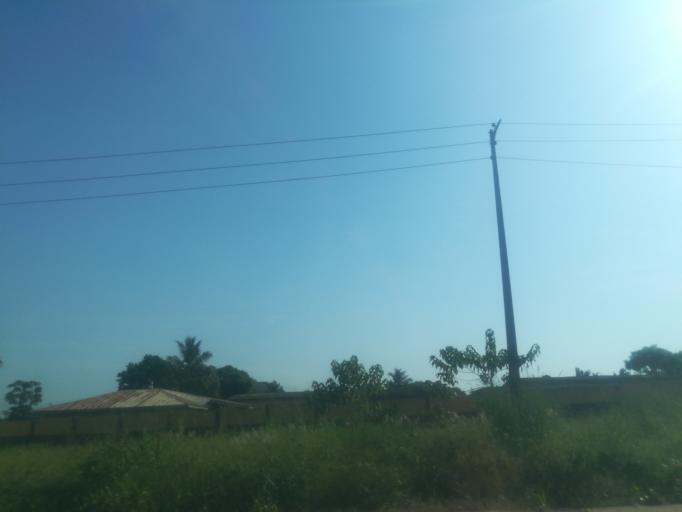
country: NG
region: Ogun
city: Abeokuta
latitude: 7.1367
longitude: 3.2935
